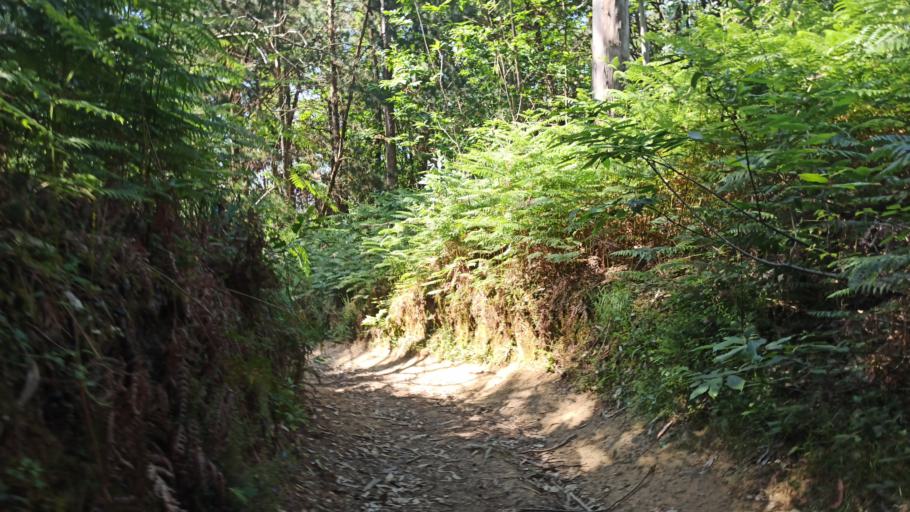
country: ES
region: Galicia
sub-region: Provincia da Coruna
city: Sada
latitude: 43.3828
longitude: -8.2708
